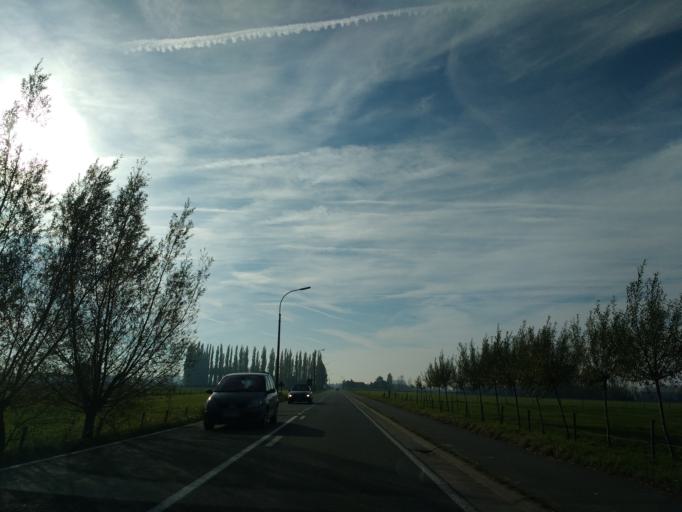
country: BE
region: Flanders
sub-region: Provincie Oost-Vlaanderen
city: Kaprijke
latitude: 51.2676
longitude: 3.6184
